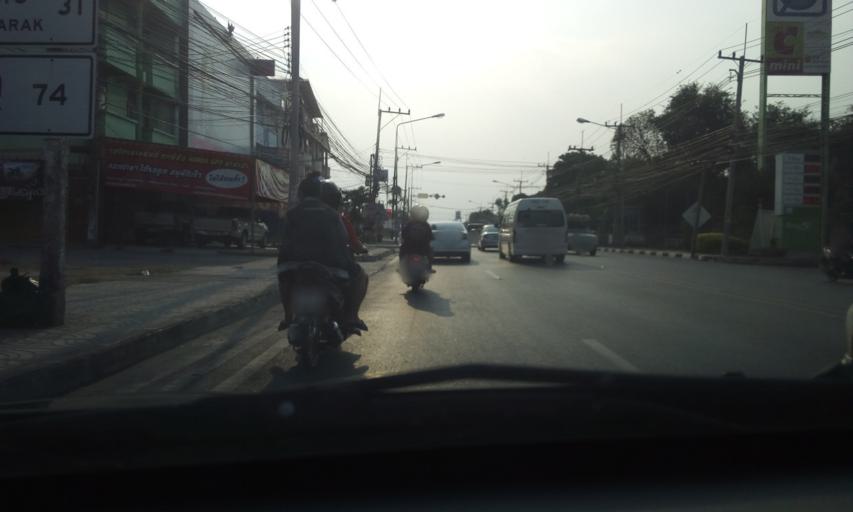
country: TH
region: Nakhon Nayok
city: Nakhon Nayok
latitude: 14.2046
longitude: 101.2096
